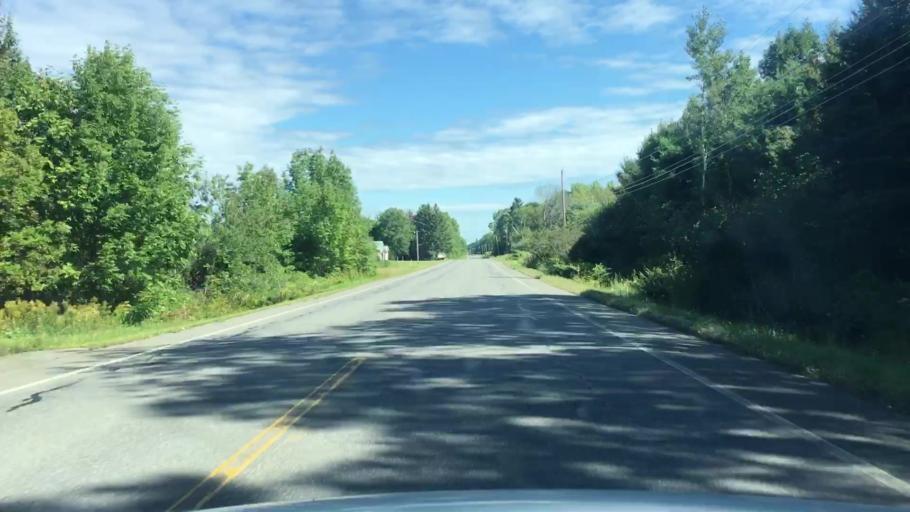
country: US
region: Maine
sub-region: Penobscot County
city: Dexter
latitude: 45.0612
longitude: -69.2491
